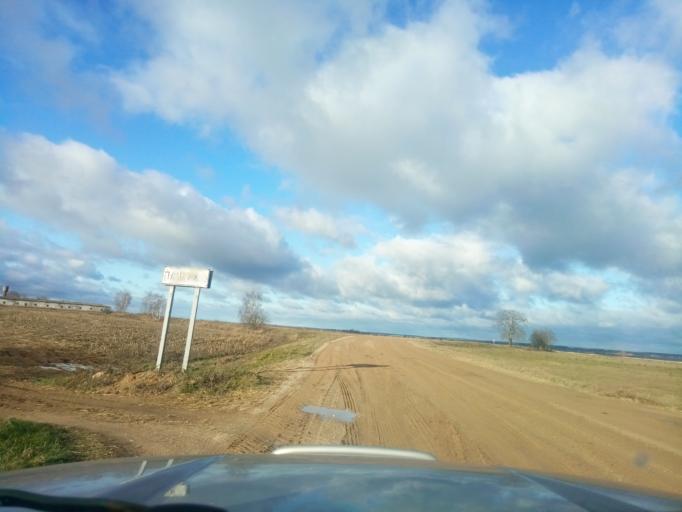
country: BY
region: Minsk
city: Tsimkavichy
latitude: 53.1826
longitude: 26.9471
